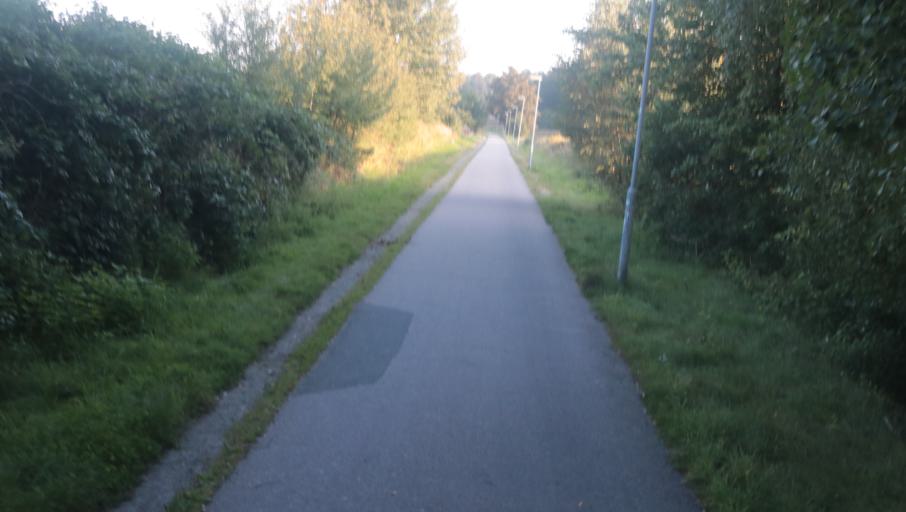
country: SE
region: Blekinge
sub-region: Karlshamns Kommun
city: Karlshamn
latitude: 56.1943
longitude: 14.8382
